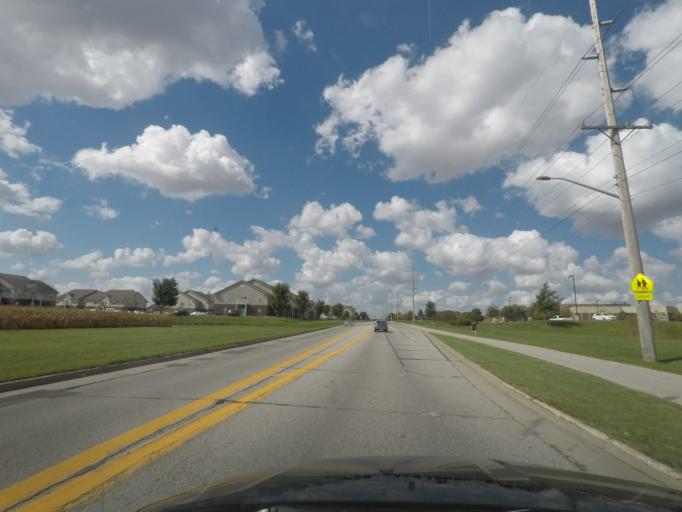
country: US
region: Iowa
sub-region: Story County
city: Ames
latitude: 42.0120
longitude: -93.6681
